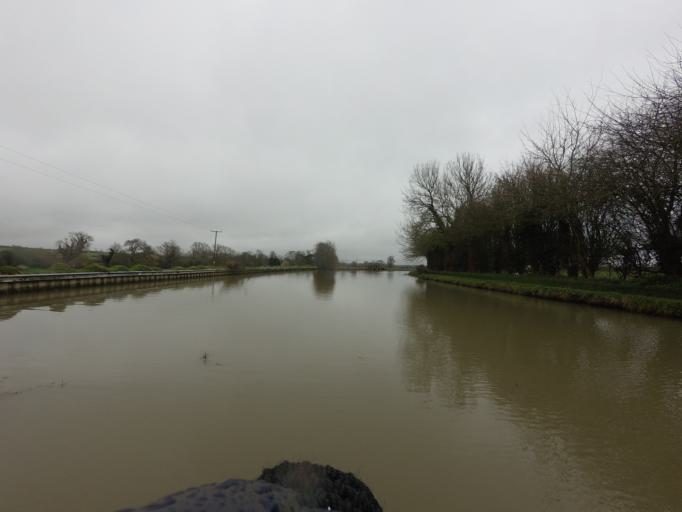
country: GB
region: England
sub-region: Milton Keynes
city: Castlethorpe
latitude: 52.0832
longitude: -0.8451
